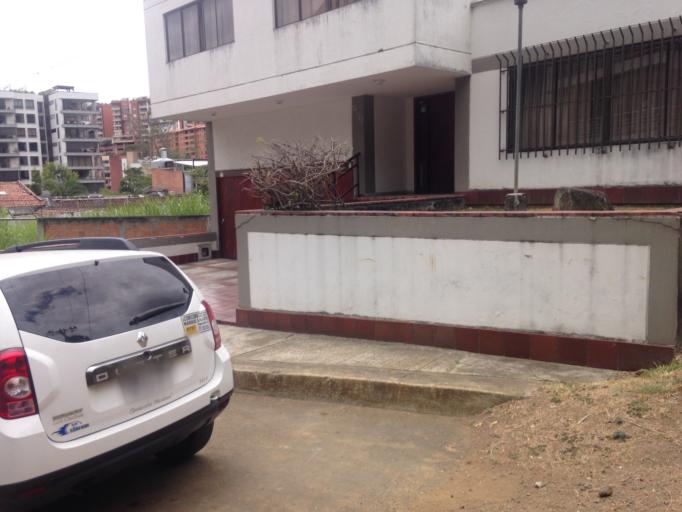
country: CO
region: Valle del Cauca
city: Cali
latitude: 3.4494
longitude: -76.5571
